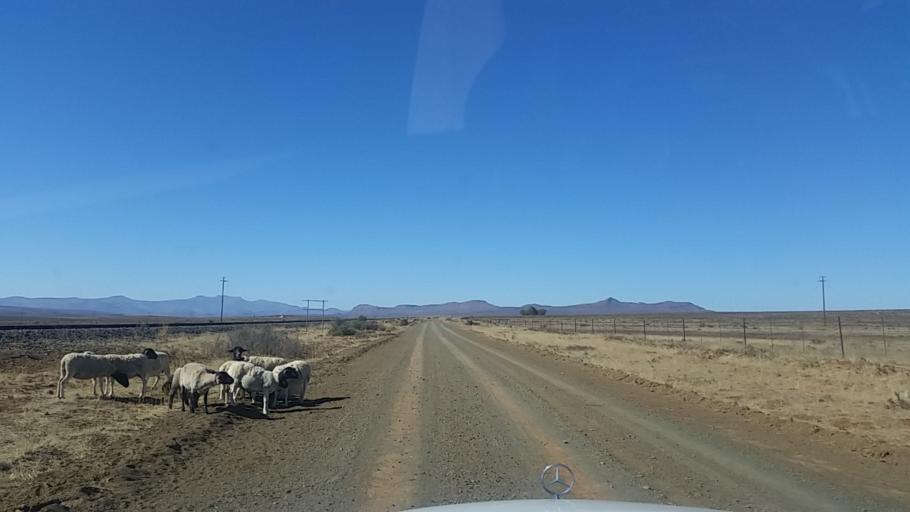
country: ZA
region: Eastern Cape
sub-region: Cacadu District Municipality
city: Graaff-Reinet
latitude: -31.8953
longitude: 24.7589
